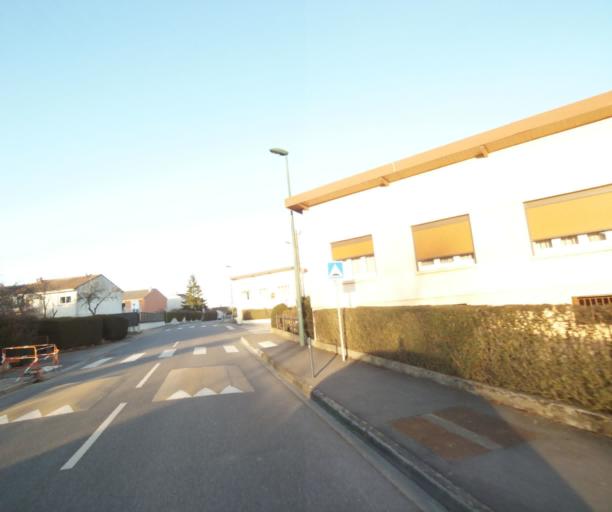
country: FR
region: Lorraine
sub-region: Departement de Meurthe-et-Moselle
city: Saulxures-les-Nancy
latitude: 48.6916
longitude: 6.2488
